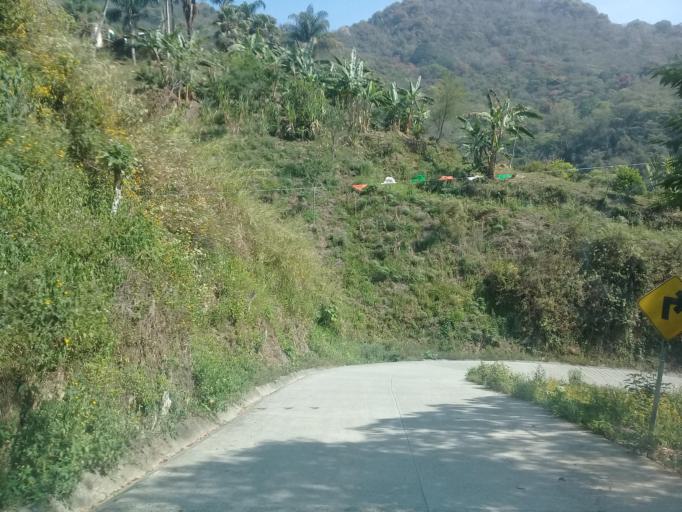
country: MX
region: Veracruz
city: Rafael Delgado
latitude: 18.7824
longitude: -97.0263
